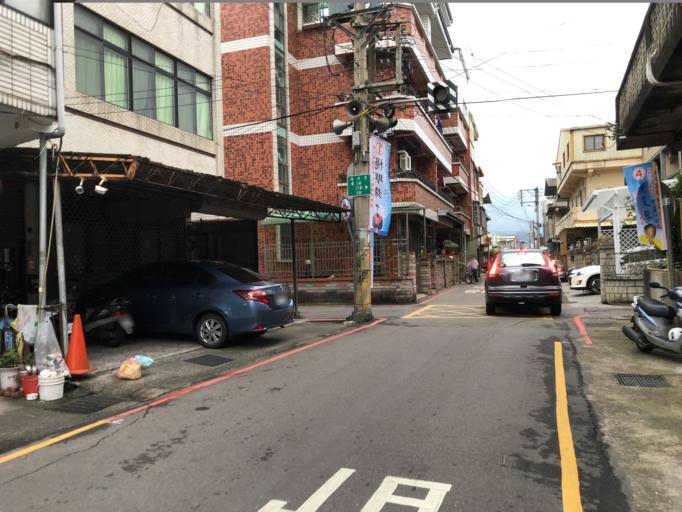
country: TW
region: Taiwan
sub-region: Miaoli
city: Miaoli
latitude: 24.5546
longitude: 120.8229
